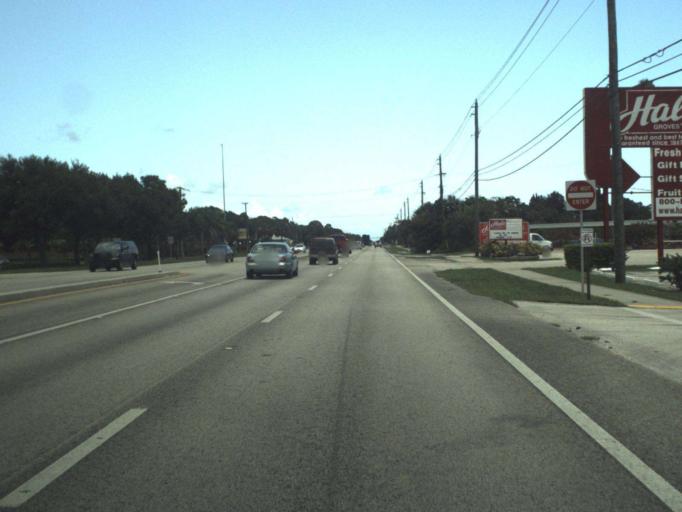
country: US
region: Florida
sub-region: Indian River County
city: Wabasso Beach
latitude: 27.7613
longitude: -80.4406
